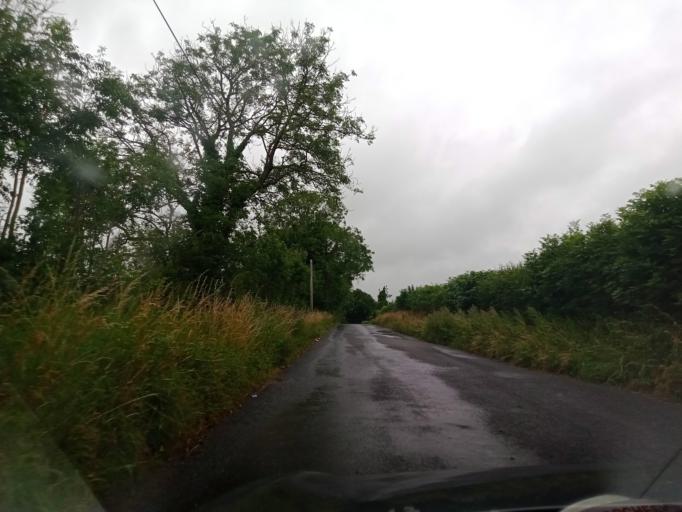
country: IE
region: Leinster
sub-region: Laois
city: Abbeyleix
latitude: 52.9169
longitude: -7.2888
